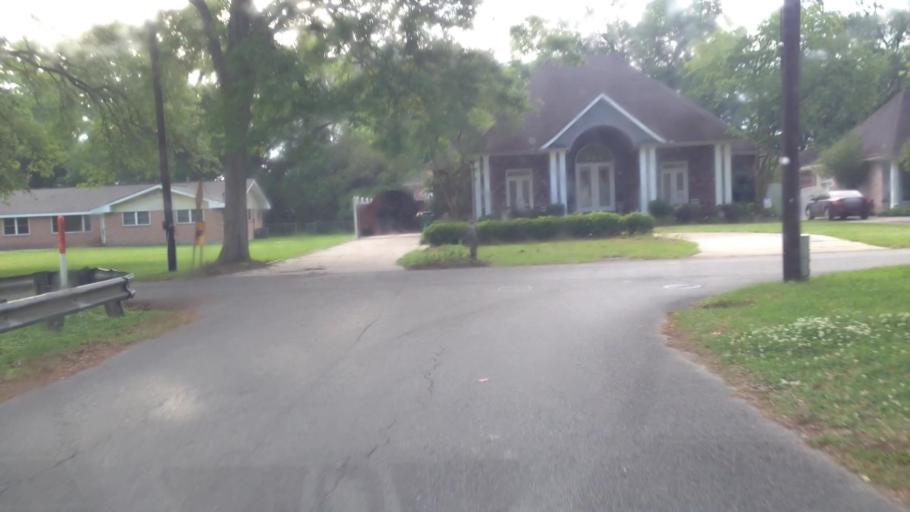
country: US
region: Louisiana
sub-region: Jefferson Parish
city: Jefferson
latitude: 29.9493
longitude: -90.1514
